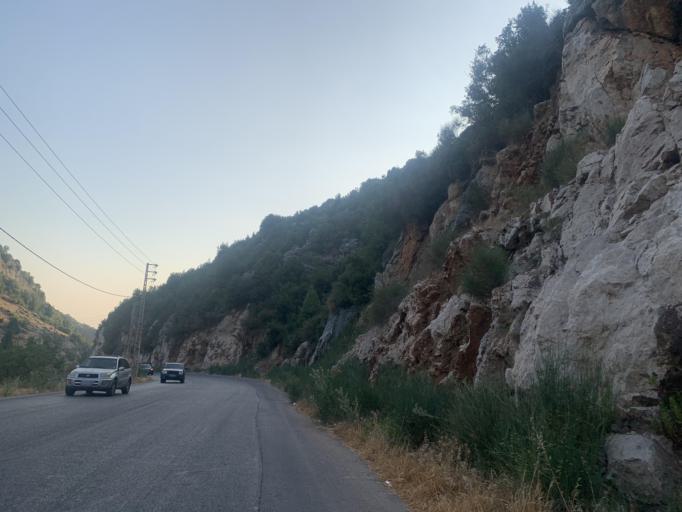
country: LB
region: Mont-Liban
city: Jbail
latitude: 34.1294
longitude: 35.8109
